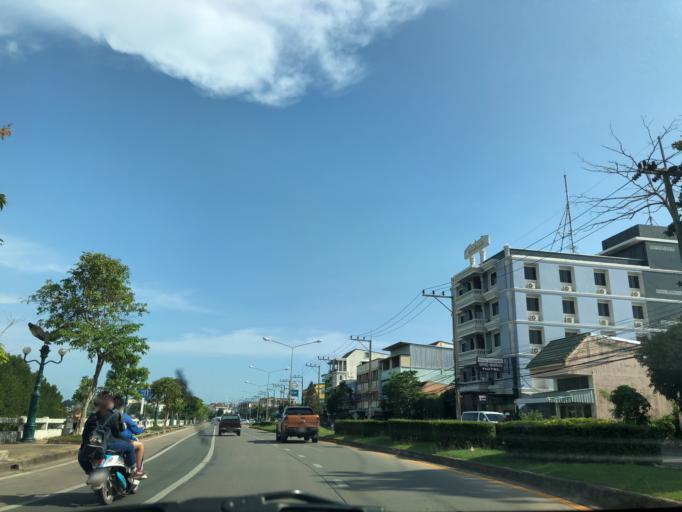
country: TH
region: Krabi
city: Krabi
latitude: 8.0719
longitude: 98.9165
